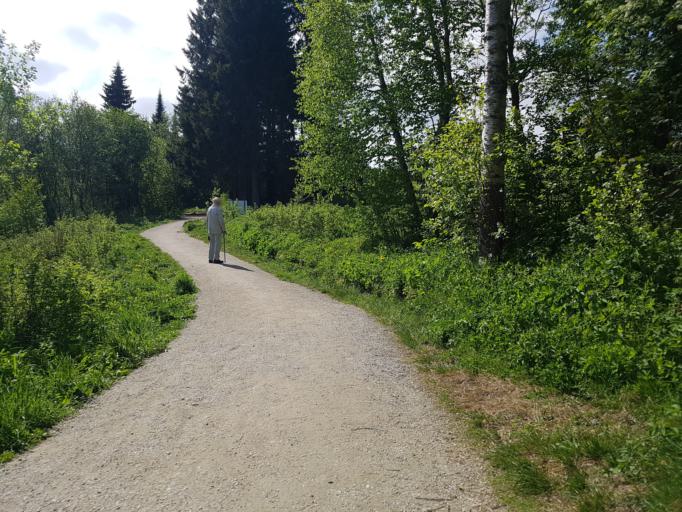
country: NO
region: Sor-Trondelag
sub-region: Trondheim
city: Trondheim
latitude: 63.4203
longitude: 10.3409
